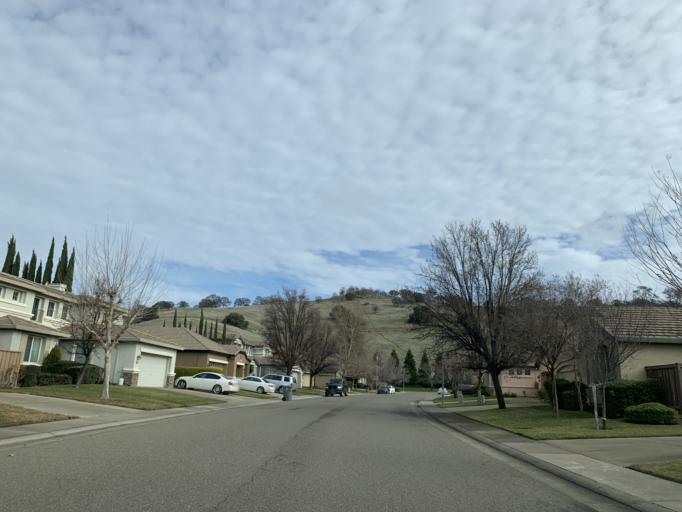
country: US
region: California
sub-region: El Dorado County
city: El Dorado Hills
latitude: 38.6773
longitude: -121.1022
